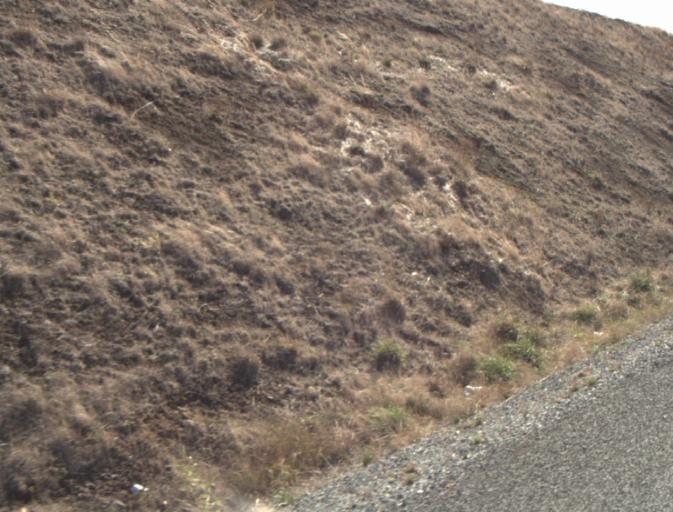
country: AU
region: Tasmania
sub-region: Launceston
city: Mayfield
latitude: -41.3555
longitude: 147.1046
